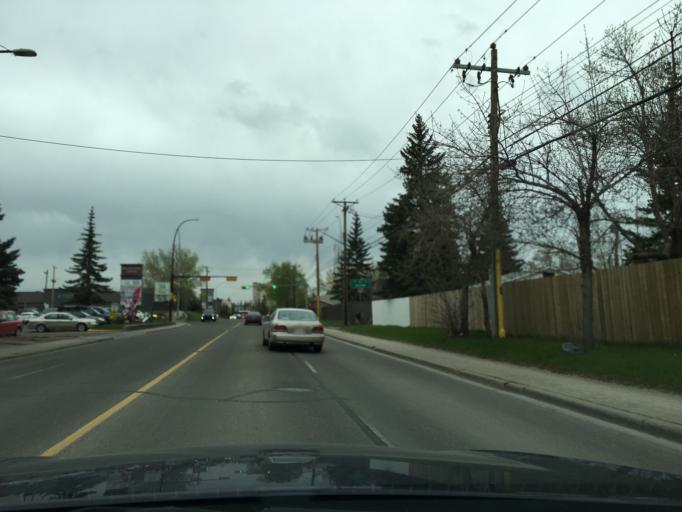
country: CA
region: Alberta
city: Calgary
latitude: 50.9601
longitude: -114.0689
